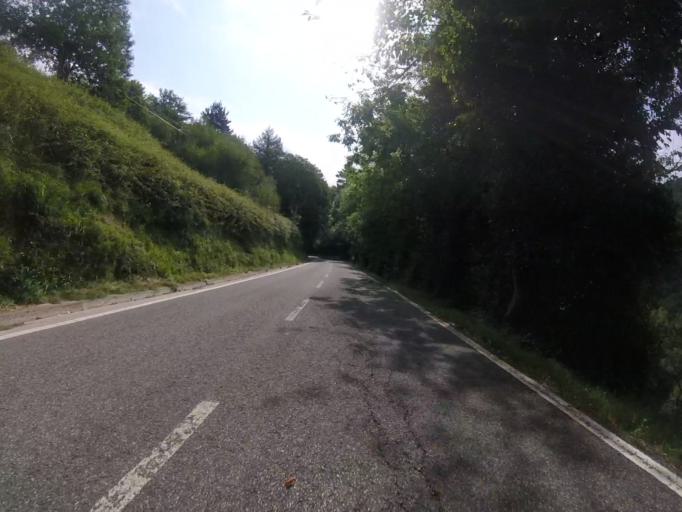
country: ES
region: Navarre
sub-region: Provincia de Navarra
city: Ezkurra
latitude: 43.0831
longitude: -1.8186
